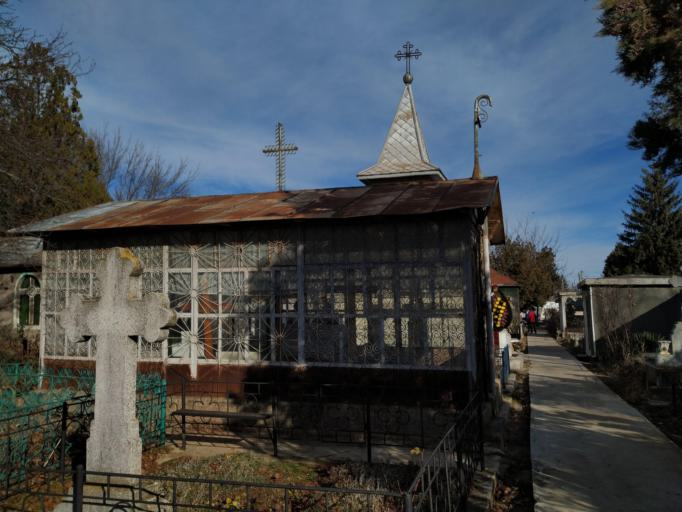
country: RO
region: Ilfov
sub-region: Comuna Popesti-Leordeni
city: Popesti-Leordeni
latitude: 44.3831
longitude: 26.1635
